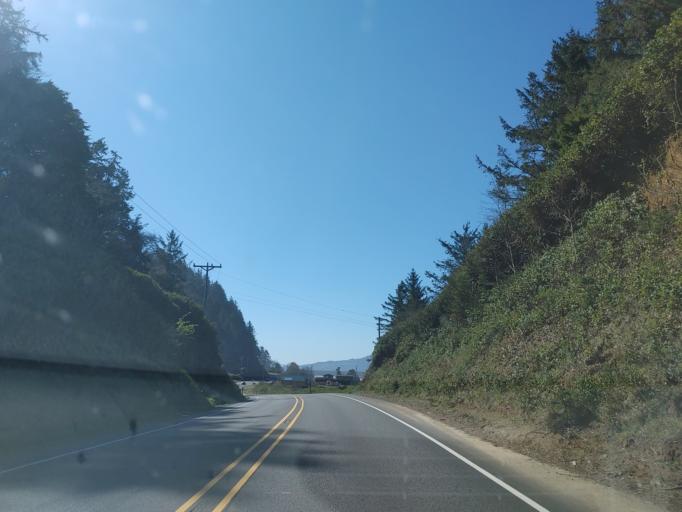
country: US
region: Oregon
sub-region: Tillamook County
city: Rockaway Beach
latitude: 45.5732
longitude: -123.9441
